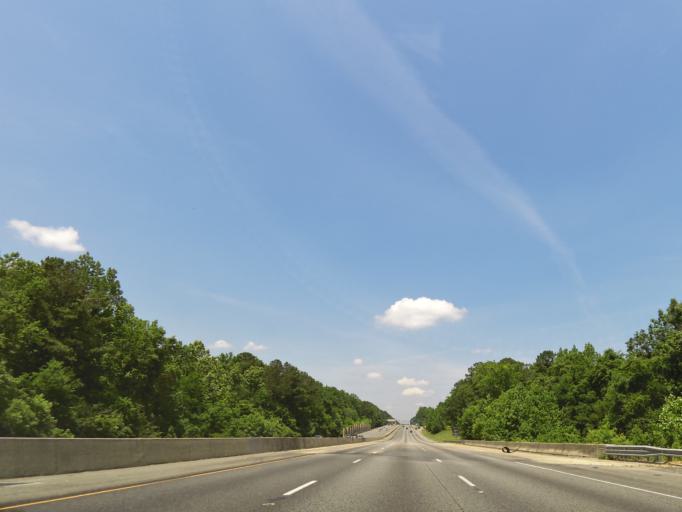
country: US
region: Georgia
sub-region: Bibb County
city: West Point
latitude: 32.8609
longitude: -83.7481
